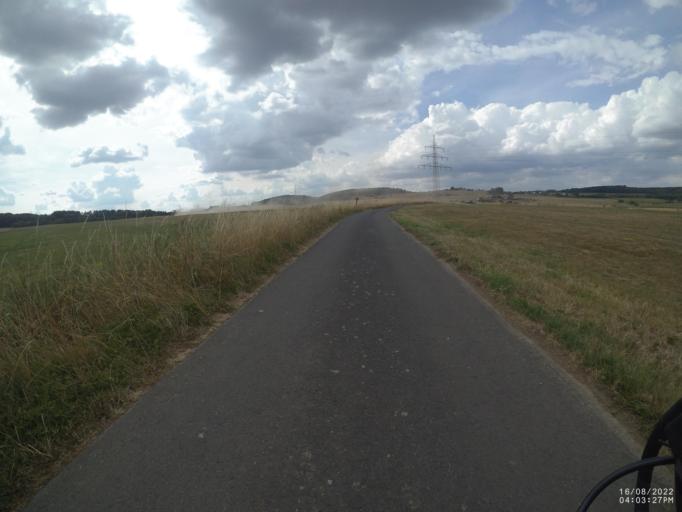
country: DE
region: Rheinland-Pfalz
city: Walsdorf
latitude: 50.2964
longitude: 6.7164
